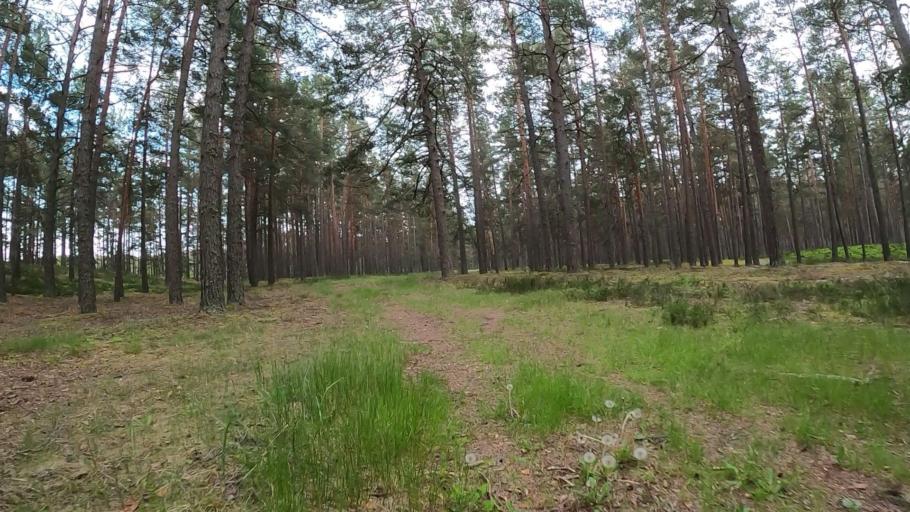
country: LV
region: Carnikava
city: Carnikava
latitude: 57.1680
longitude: 24.3258
